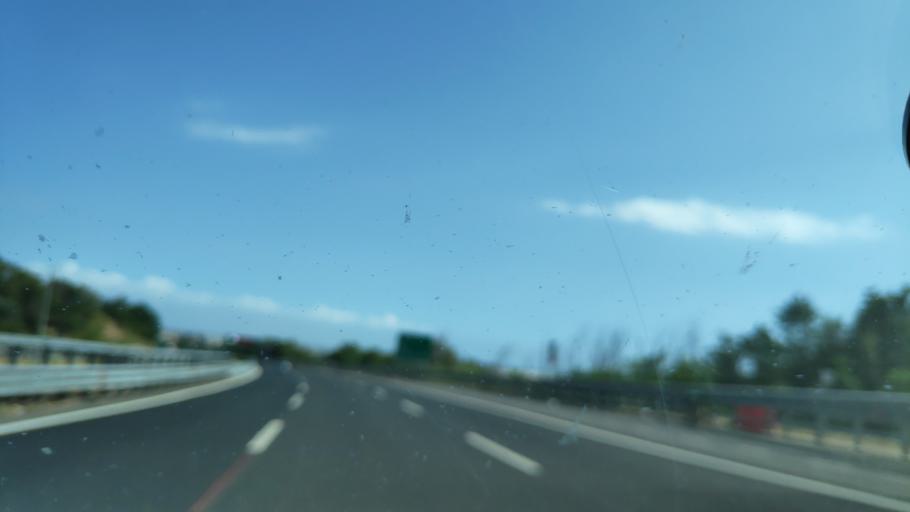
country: IT
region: Campania
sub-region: Provincia di Salerno
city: Fuorni
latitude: 40.6627
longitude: 14.8589
